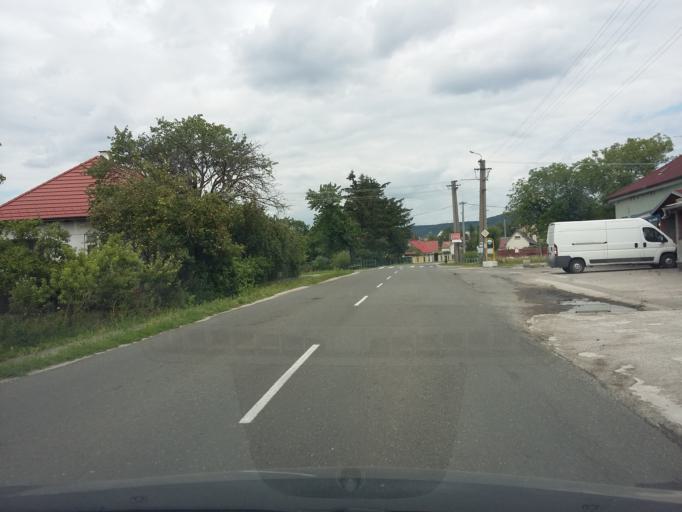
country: SK
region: Trnavsky
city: Smolenice
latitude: 48.5335
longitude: 17.3217
